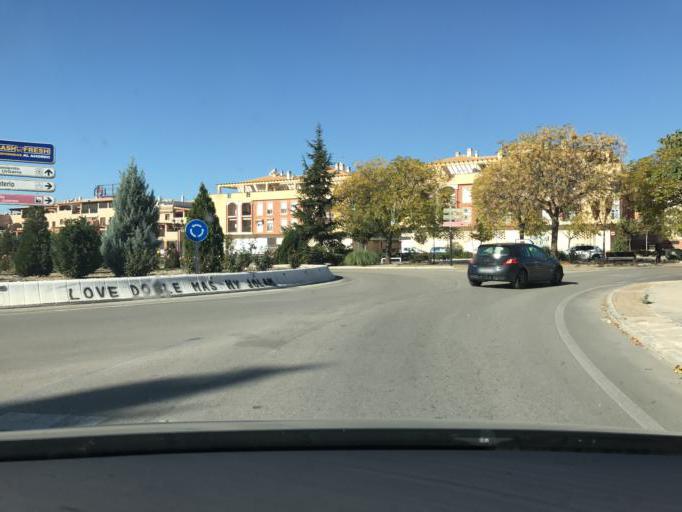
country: ES
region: Andalusia
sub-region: Provincia de Granada
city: Atarfe
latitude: 37.2247
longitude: -3.6784
